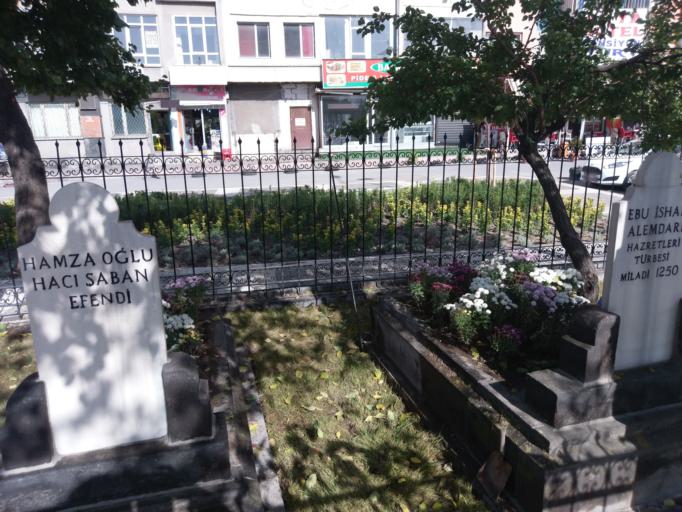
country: TR
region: Kayseri
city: Kayseri
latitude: 38.7174
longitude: 35.4923
